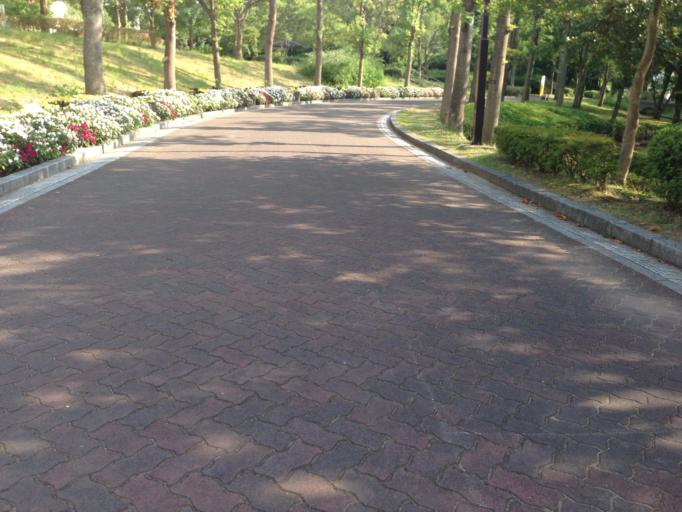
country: JP
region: Hyogo
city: Kobe
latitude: 34.7064
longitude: 135.1145
